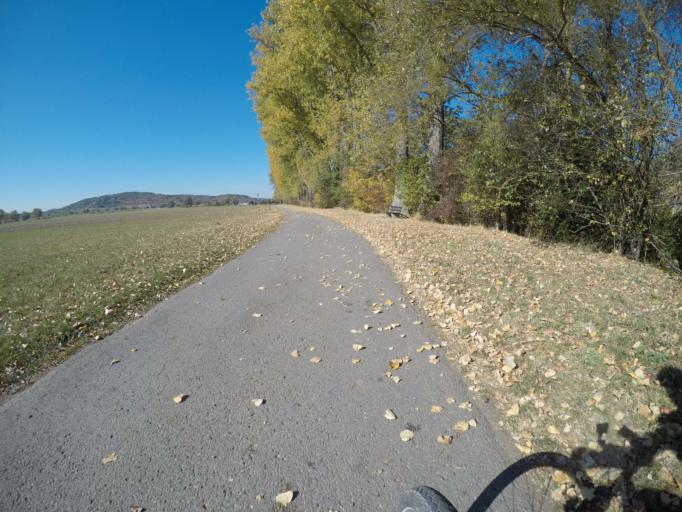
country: DE
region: Baden-Wuerttemberg
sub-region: Tuebingen Region
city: Tuebingen
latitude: 48.5218
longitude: 8.9868
